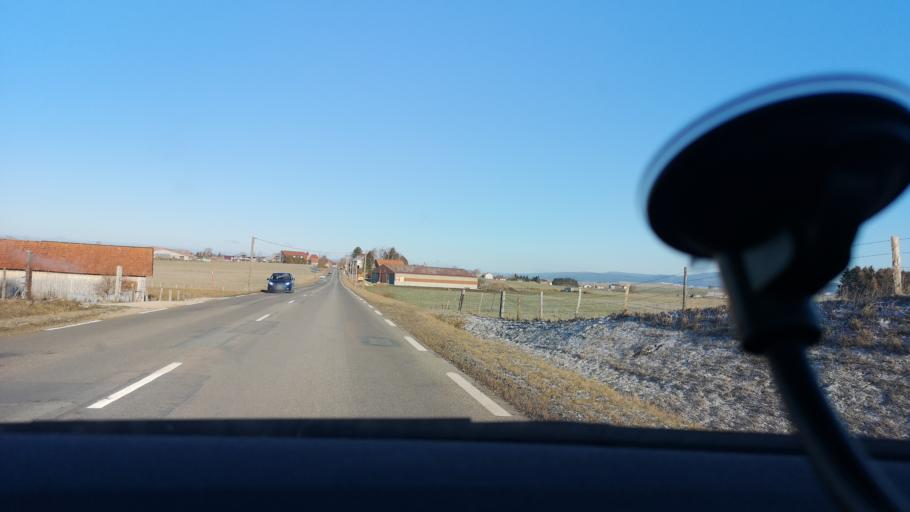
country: FR
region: Franche-Comte
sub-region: Departement du Doubs
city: Frasne
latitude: 46.8650
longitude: 6.1740
